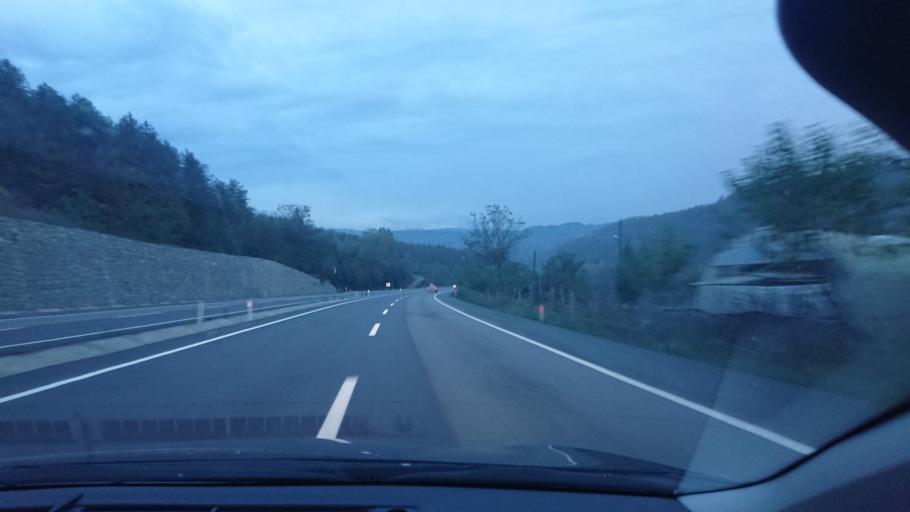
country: TR
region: Zonguldak
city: Beycuma
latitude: 41.3328
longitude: 32.0437
